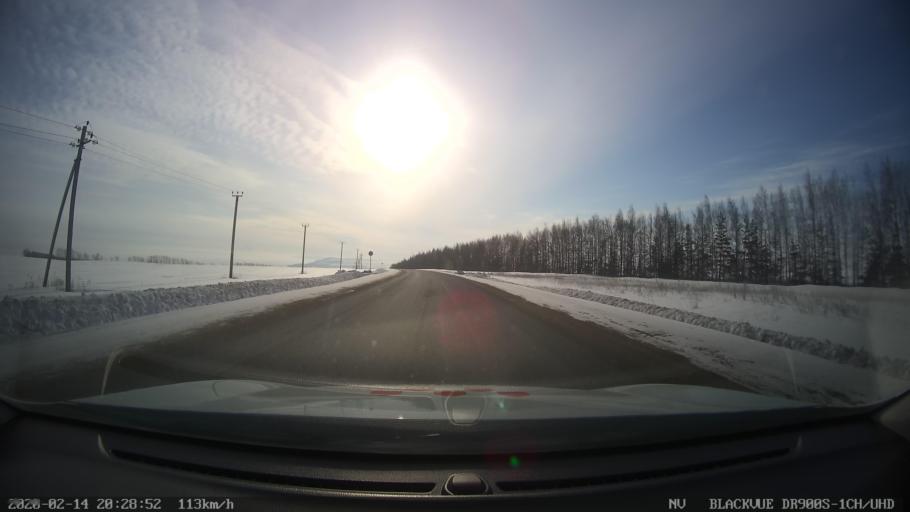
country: RU
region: Tatarstan
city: Stolbishchi
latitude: 55.4566
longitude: 48.9778
